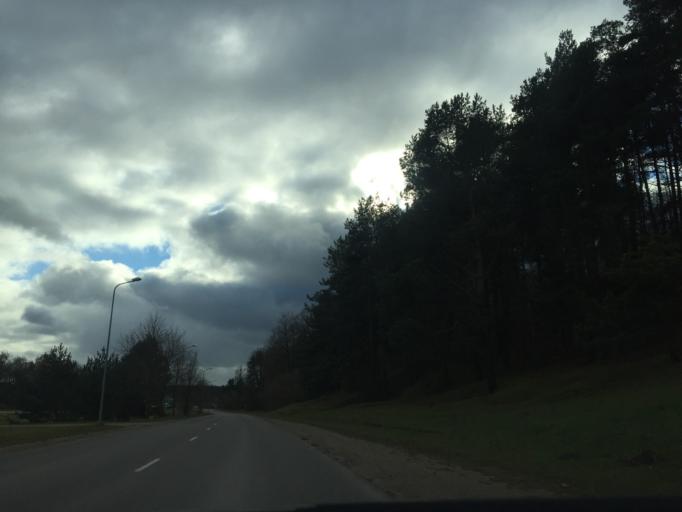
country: LV
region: Tukuma Rajons
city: Tukums
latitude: 56.9662
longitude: 23.1376
